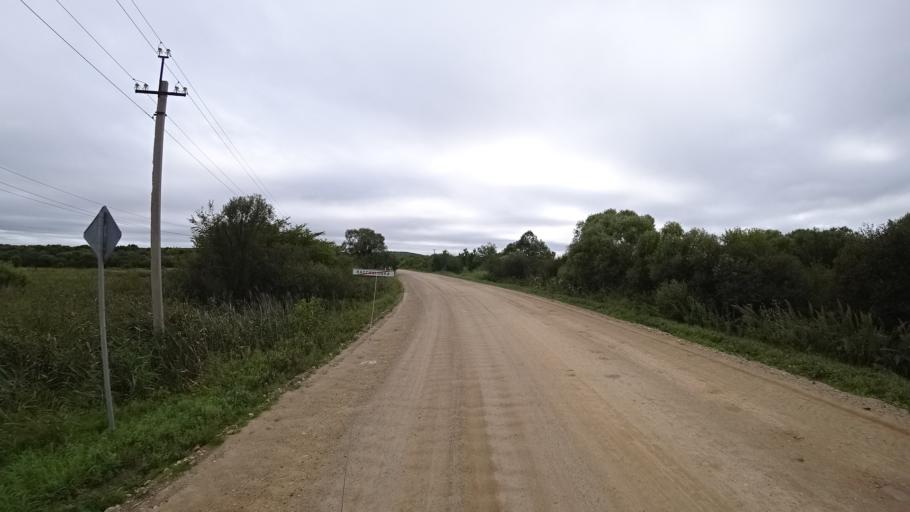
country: RU
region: Primorskiy
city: Rettikhovka
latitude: 44.1303
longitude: 132.6430
